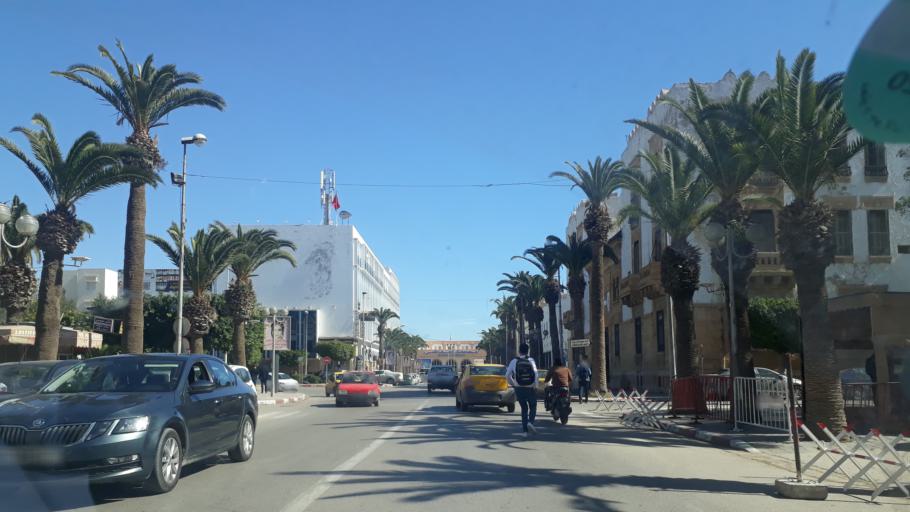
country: TN
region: Safaqis
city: Sfax
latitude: 34.7337
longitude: 10.7653
